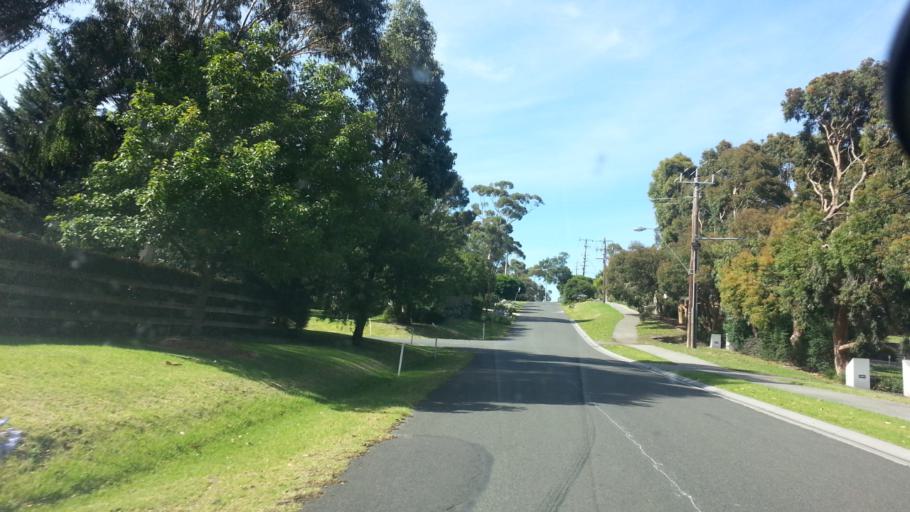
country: AU
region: Victoria
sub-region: Casey
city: Endeavour Hills
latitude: -37.9602
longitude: 145.2825
